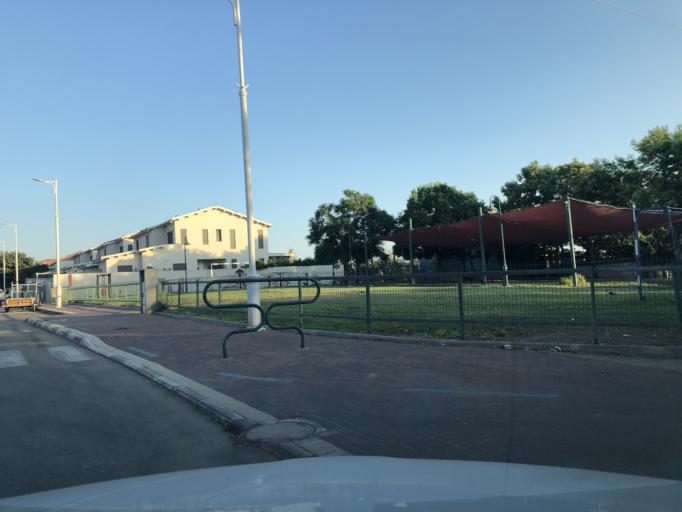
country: PS
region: West Bank
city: Hablah
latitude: 32.1604
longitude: 34.9686
